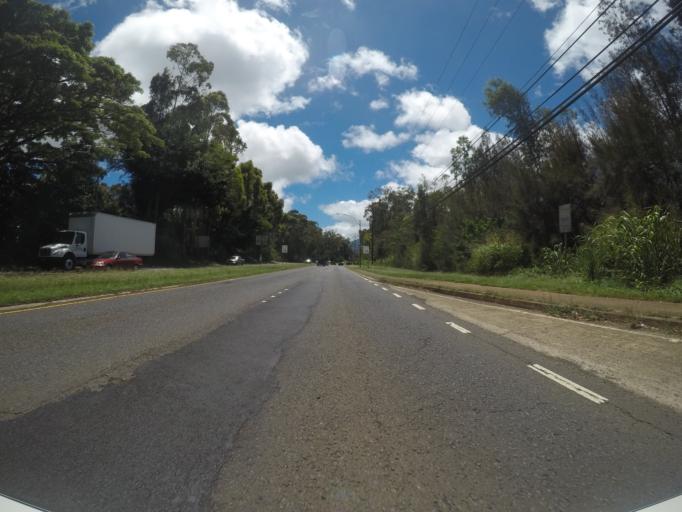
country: US
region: Hawaii
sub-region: Honolulu County
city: Wahiawa
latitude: 21.4888
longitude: -158.0405
